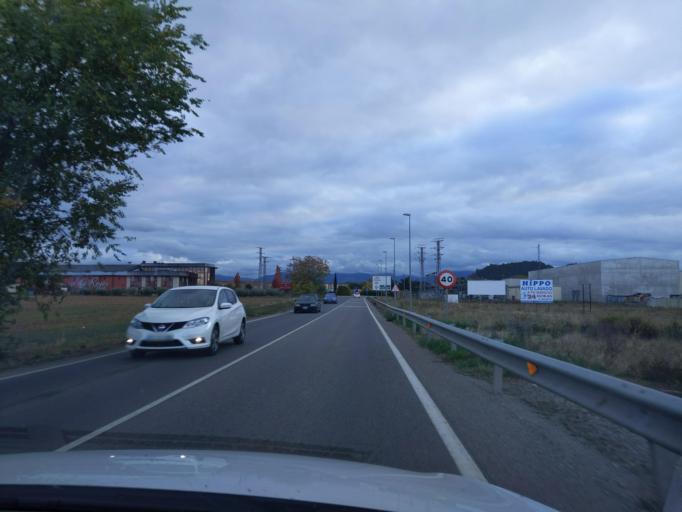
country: ES
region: La Rioja
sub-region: Provincia de La Rioja
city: Najera
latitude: 42.4260
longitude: -2.7201
